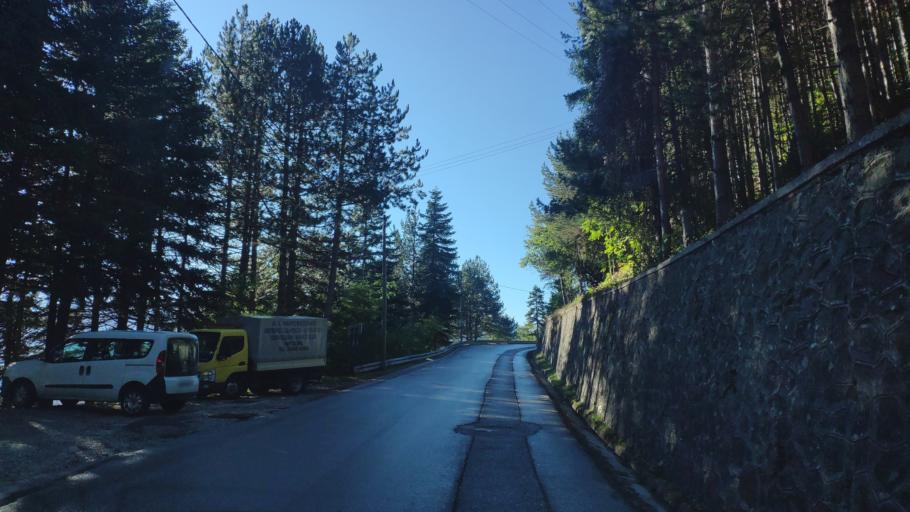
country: GR
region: Epirus
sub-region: Nomos Ioanninon
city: Metsovo
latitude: 39.7753
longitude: 21.1789
